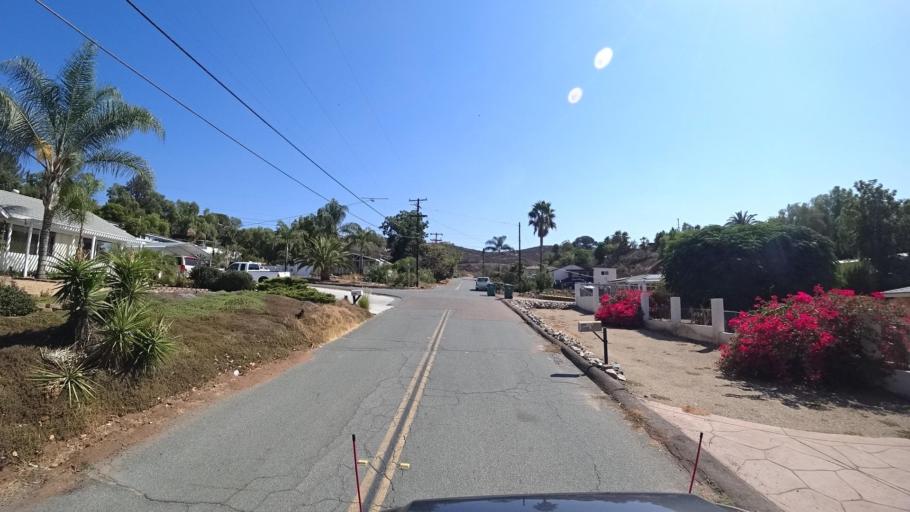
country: US
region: California
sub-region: San Diego County
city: Winter Gardens
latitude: 32.8398
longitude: -116.9306
